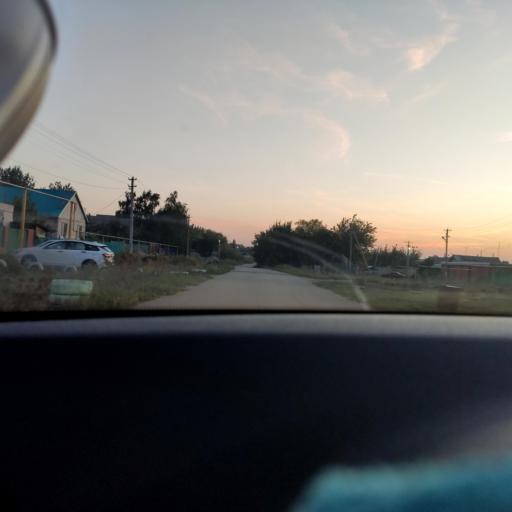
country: RU
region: Samara
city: Novokuybyshevsk
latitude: 53.0768
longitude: 50.0136
